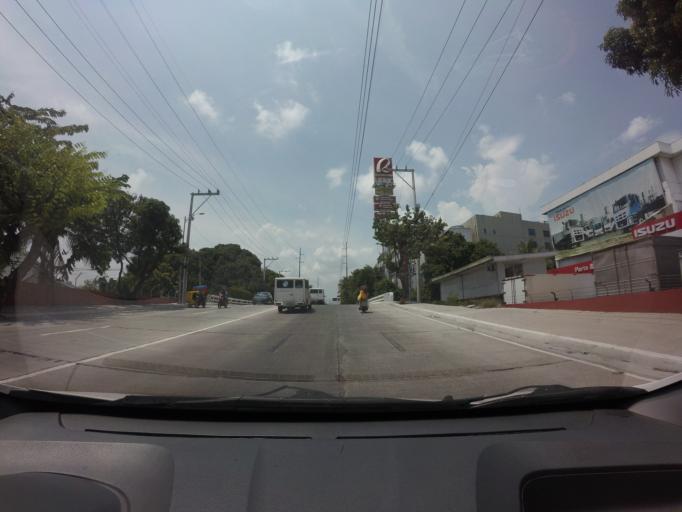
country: PH
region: Metro Manila
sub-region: City of Manila
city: Quiapo
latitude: 14.5865
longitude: 120.9947
